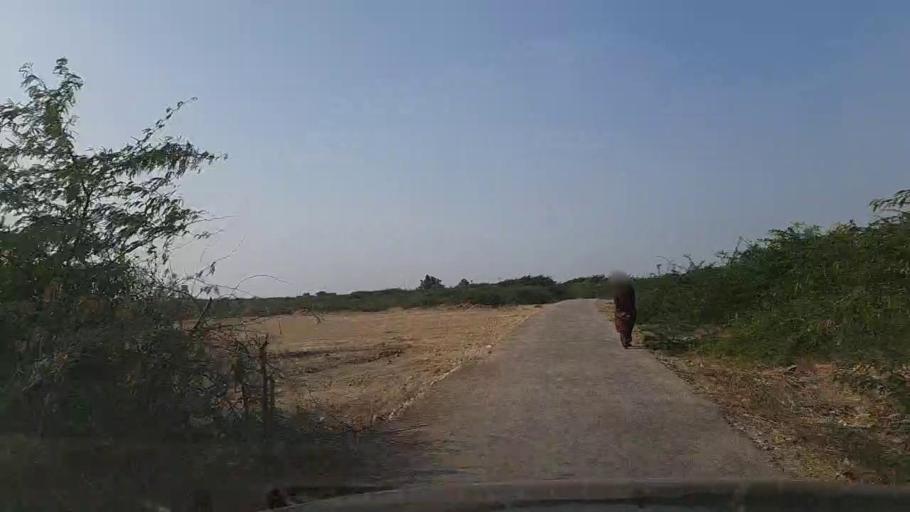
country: PK
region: Sindh
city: Gharo
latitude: 24.7565
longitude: 67.5282
